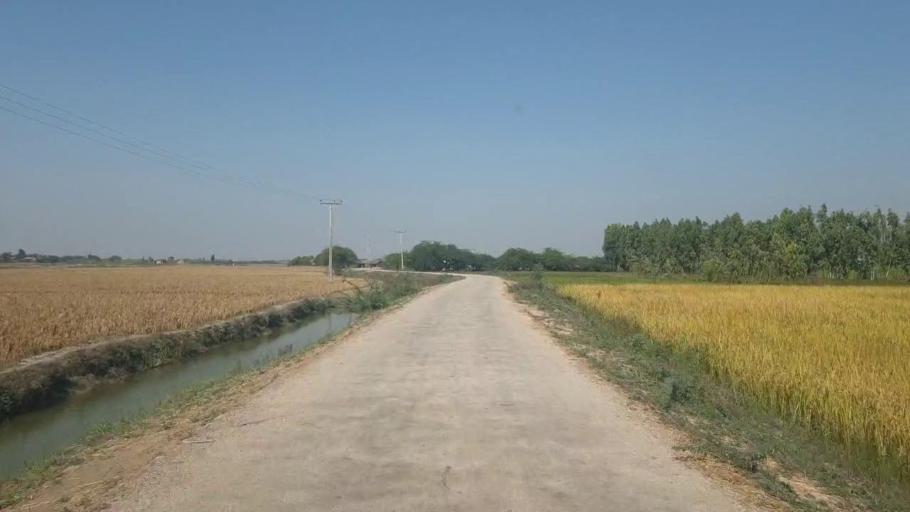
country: PK
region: Sindh
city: Badin
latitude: 24.6789
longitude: 68.9016
